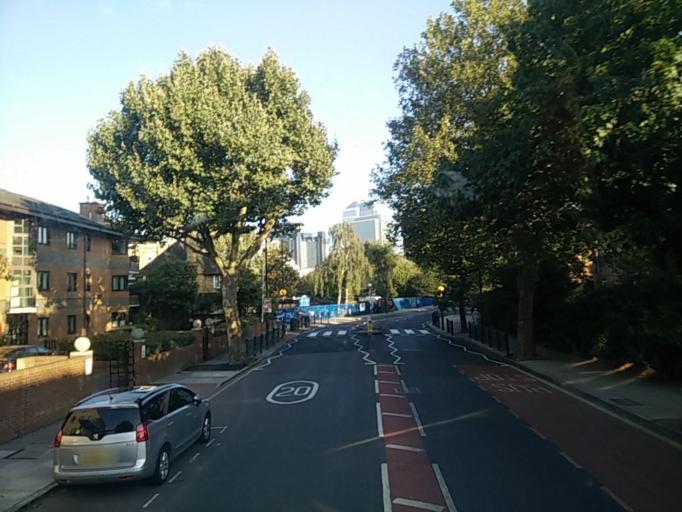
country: GB
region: England
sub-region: Greater London
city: Poplar
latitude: 51.4943
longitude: -0.0083
